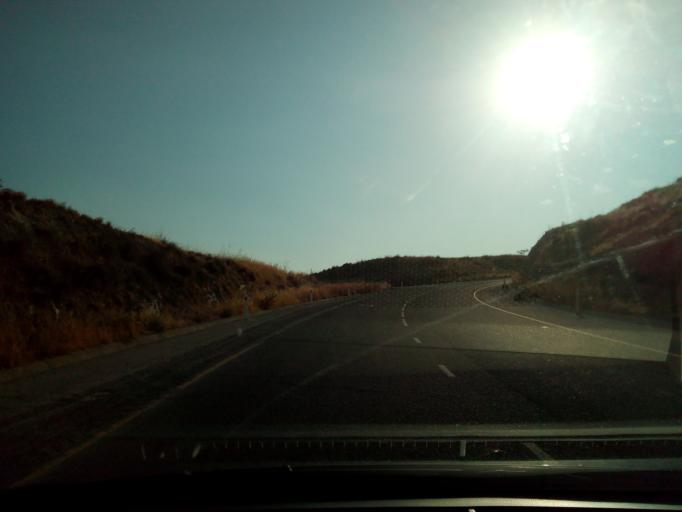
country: CY
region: Larnaka
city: Aradippou
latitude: 34.9262
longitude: 33.5658
